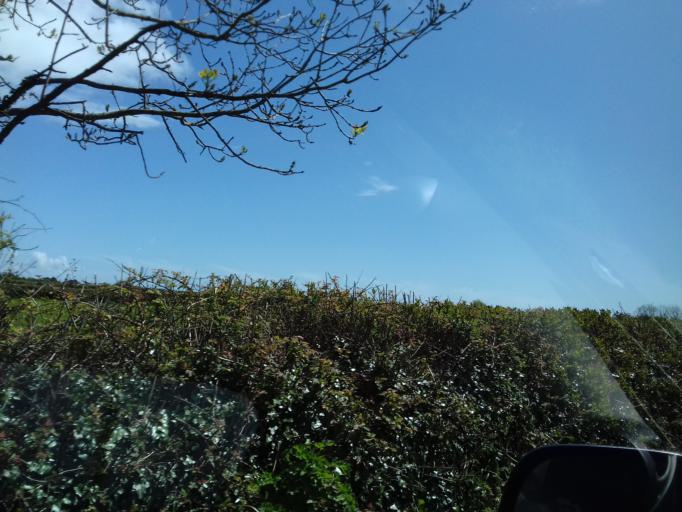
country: IE
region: Munster
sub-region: Waterford
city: Dunmore East
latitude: 52.2011
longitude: -6.8589
